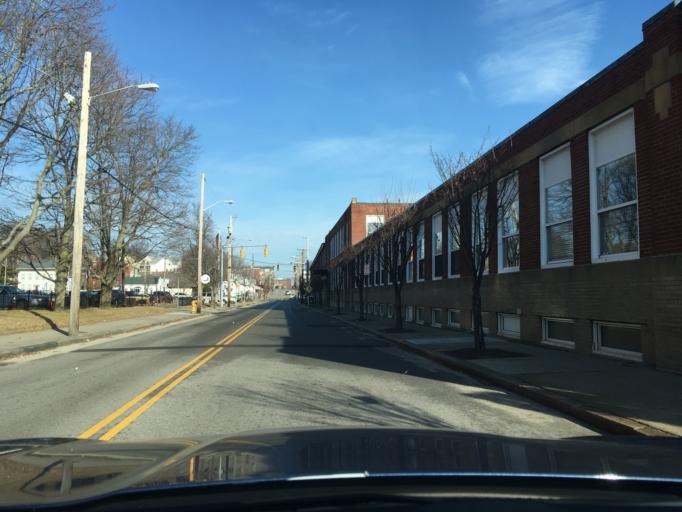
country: US
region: Rhode Island
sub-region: Providence County
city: Pawtucket
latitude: 41.8804
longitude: -71.3824
